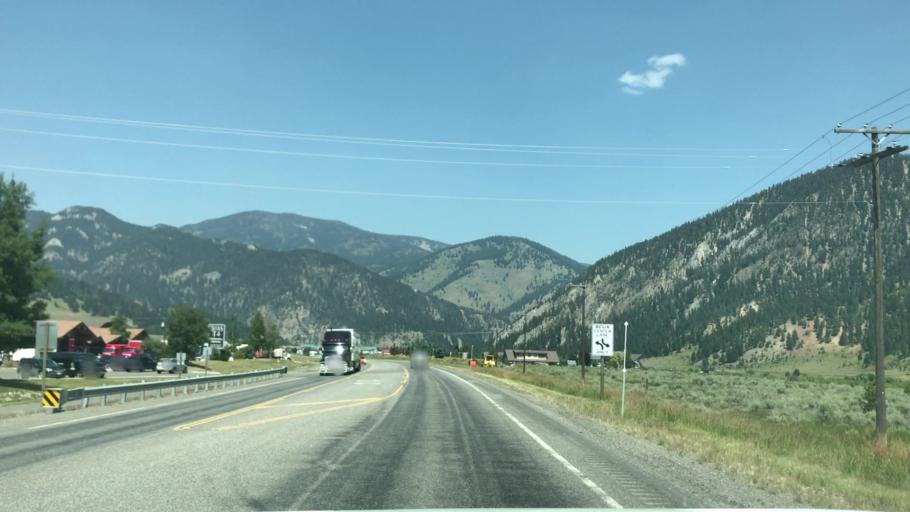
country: US
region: Montana
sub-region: Gallatin County
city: Big Sky
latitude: 45.2444
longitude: -111.2509
